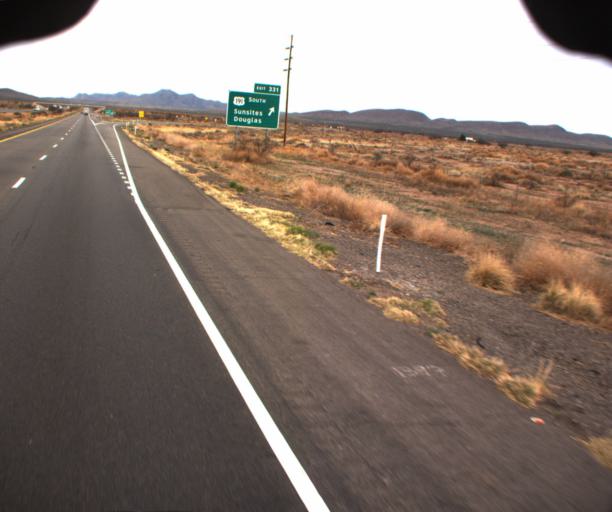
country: US
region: Arizona
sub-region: Cochise County
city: Willcox
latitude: 32.1805
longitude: -109.9431
